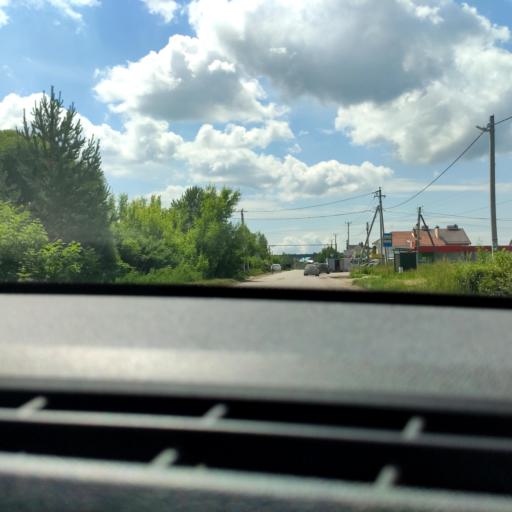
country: RU
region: Samara
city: Podstepki
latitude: 53.5715
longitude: 49.0818
